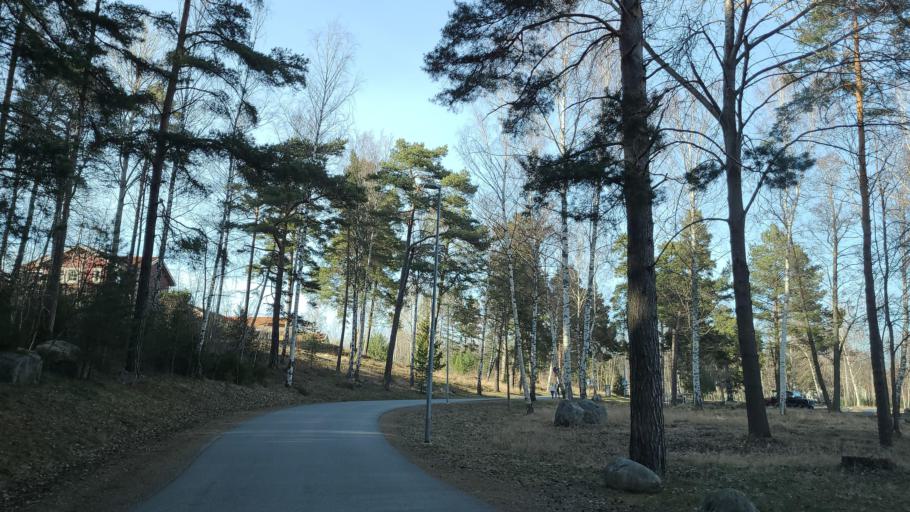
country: SE
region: Stockholm
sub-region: Ekero Kommun
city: Ekeroe
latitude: 59.2677
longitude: 17.7802
